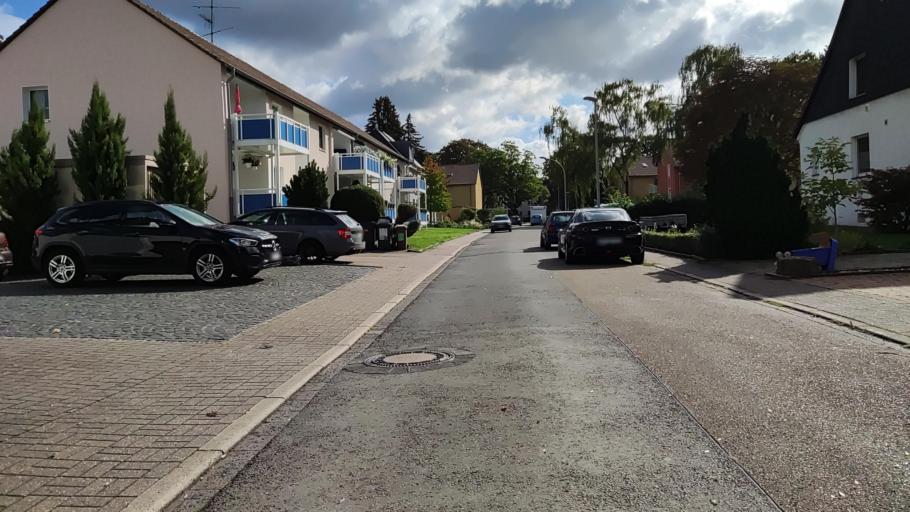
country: DE
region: North Rhine-Westphalia
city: Bochum-Hordel
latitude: 51.5191
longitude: 7.1836
